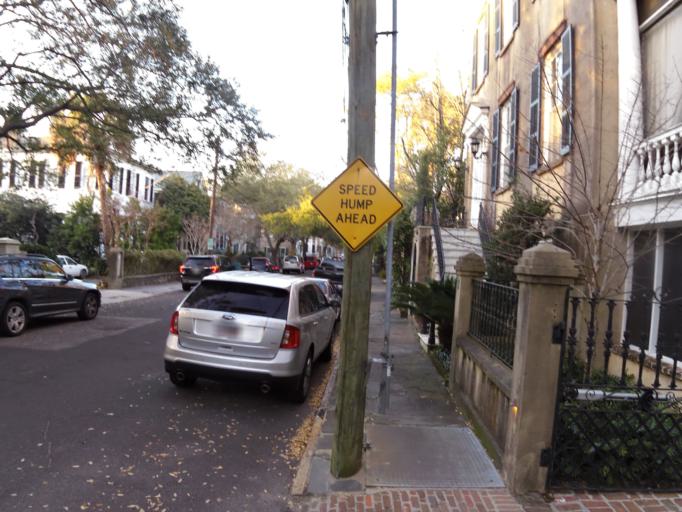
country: US
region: South Carolina
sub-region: Charleston County
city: Charleston
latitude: 32.7745
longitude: -79.9356
